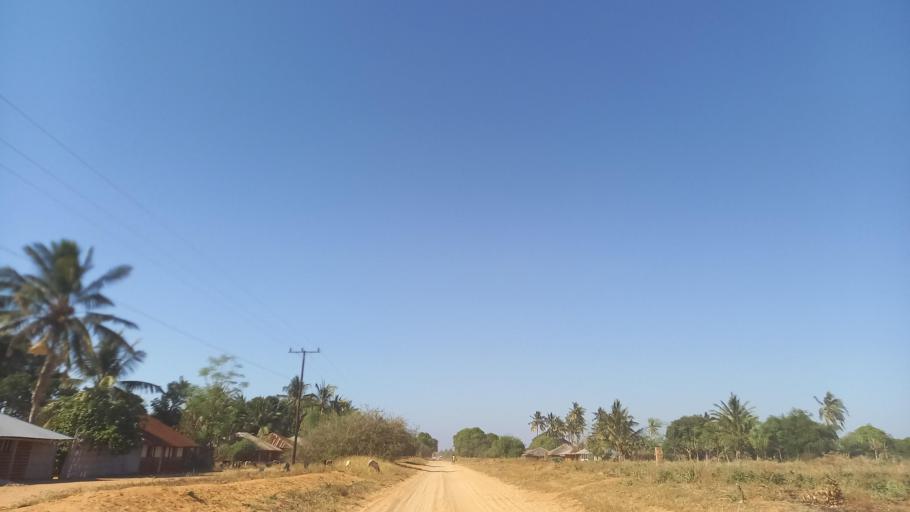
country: MZ
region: Cabo Delgado
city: Pemba
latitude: -13.1500
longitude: 40.5571
